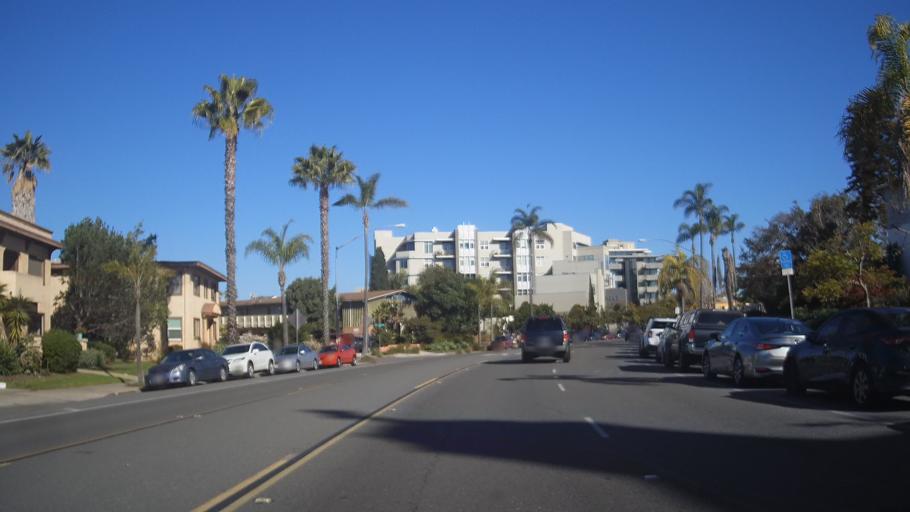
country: US
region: California
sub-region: San Diego County
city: San Diego
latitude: 32.7446
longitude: -117.1475
